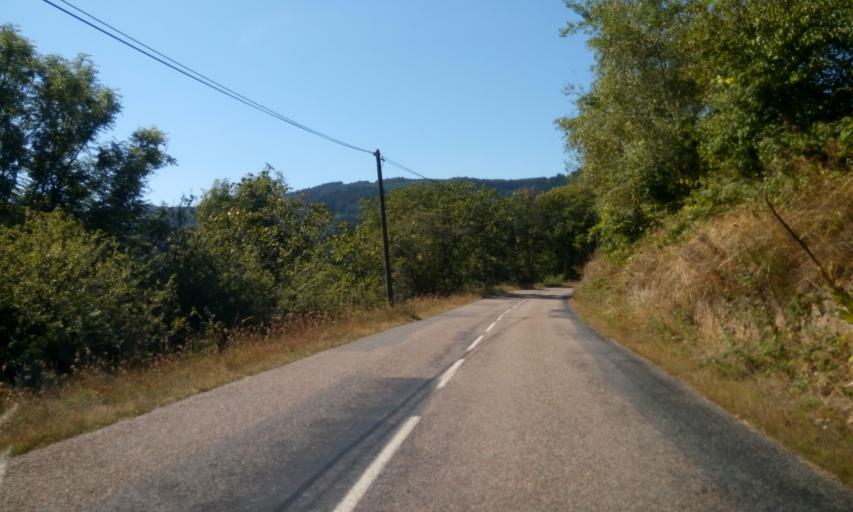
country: FR
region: Rhone-Alpes
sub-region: Departement du Rhone
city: Grandris
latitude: 46.0088
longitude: 4.4465
